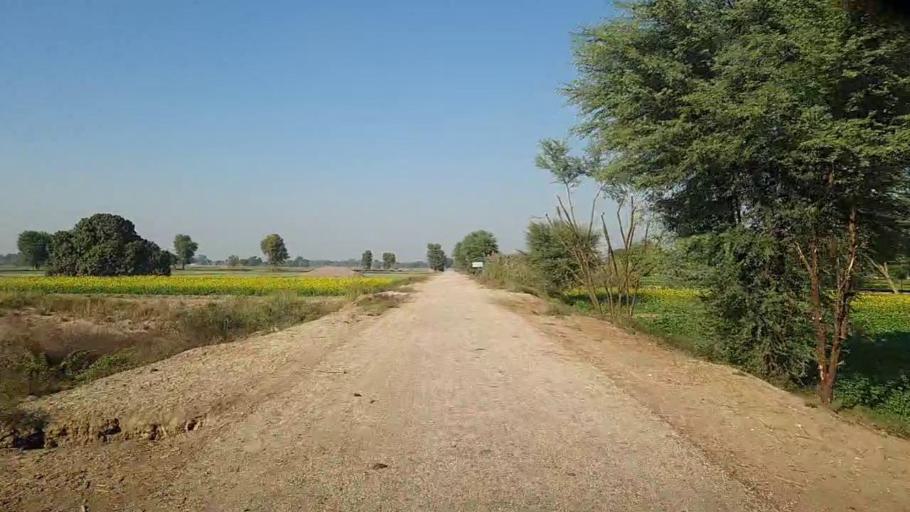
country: PK
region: Sindh
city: Darya Khan Marri
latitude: 26.6824
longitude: 68.3513
